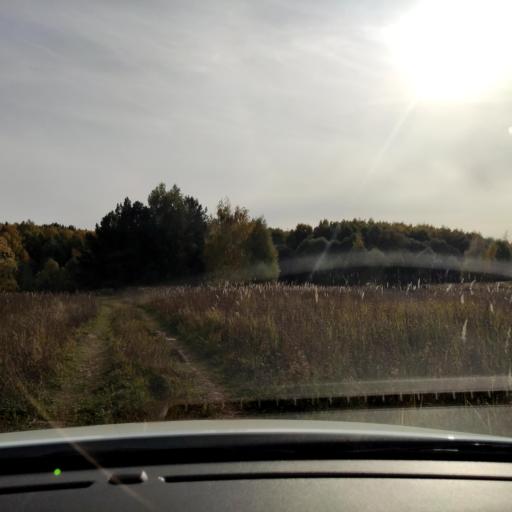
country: RU
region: Tatarstan
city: Vysokaya Gora
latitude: 55.9645
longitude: 49.2095
